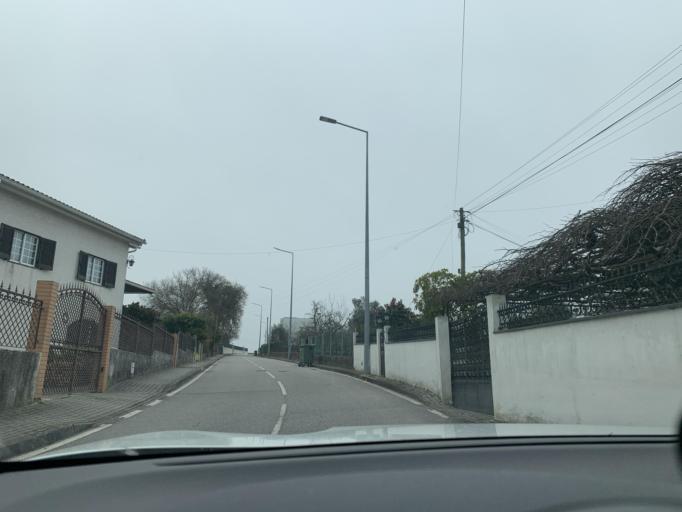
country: PT
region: Viseu
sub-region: Concelho de Tondela
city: Tondela
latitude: 40.5056
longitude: -8.0788
